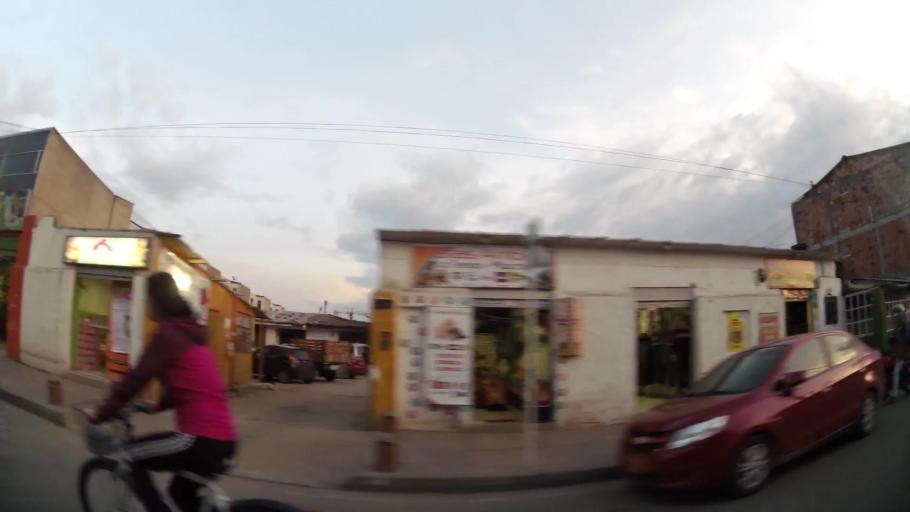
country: CO
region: Cundinamarca
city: Funza
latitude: 4.7165
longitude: -74.2084
